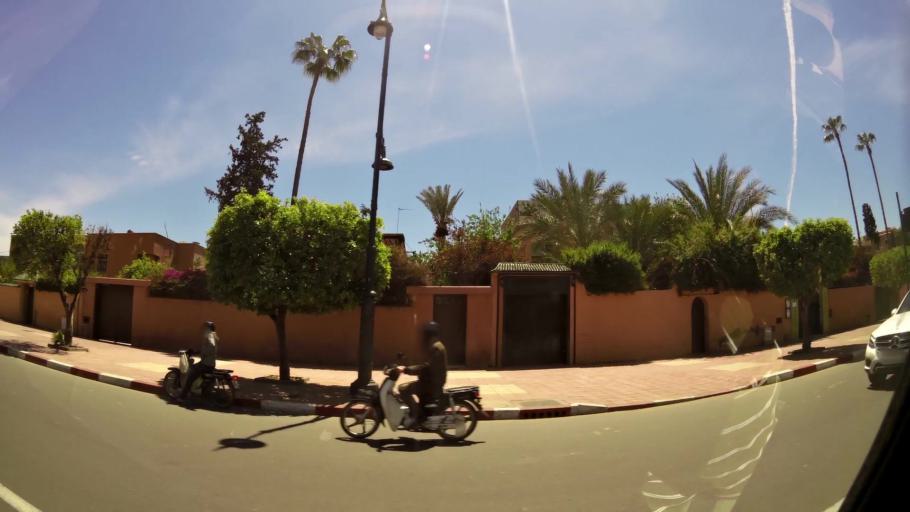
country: MA
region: Marrakech-Tensift-Al Haouz
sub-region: Marrakech
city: Marrakesh
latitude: 31.6222
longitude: -7.9943
